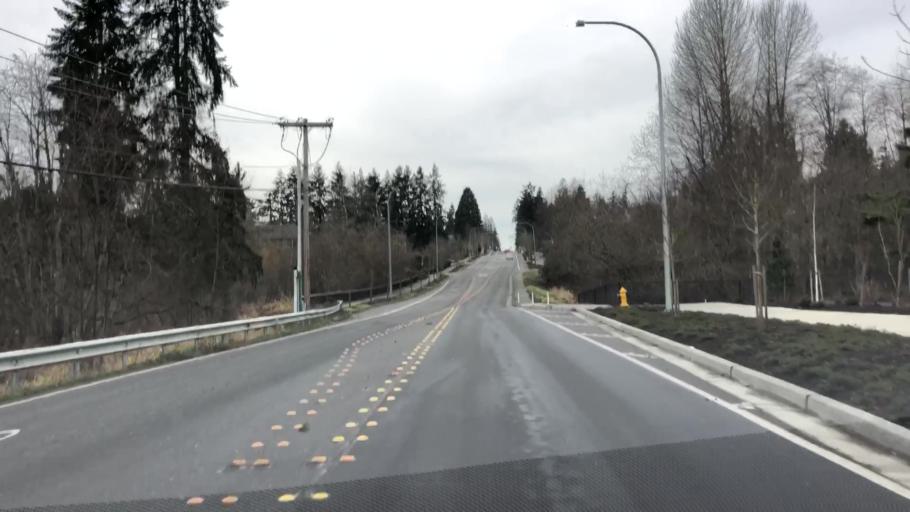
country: US
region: Washington
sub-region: King County
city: Redmond
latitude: 47.7038
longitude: -122.1033
